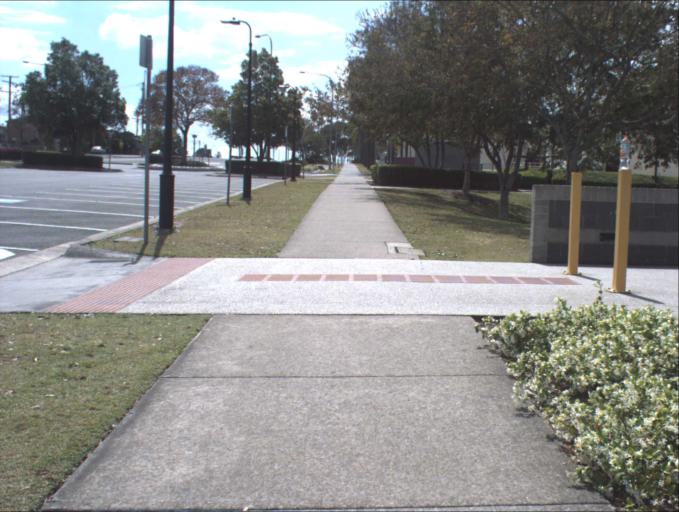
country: AU
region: Queensland
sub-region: Logan
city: Logan City
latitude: -27.6429
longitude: 153.1026
